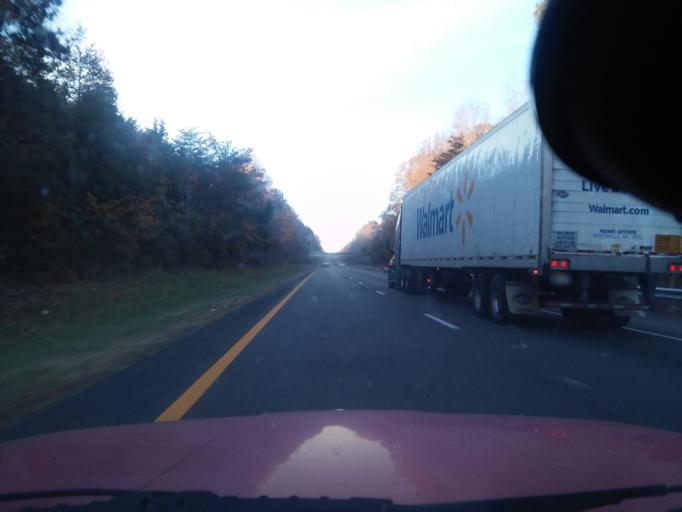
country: US
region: Virginia
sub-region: Goochland County
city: Goochland
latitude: 37.7274
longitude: -77.8214
